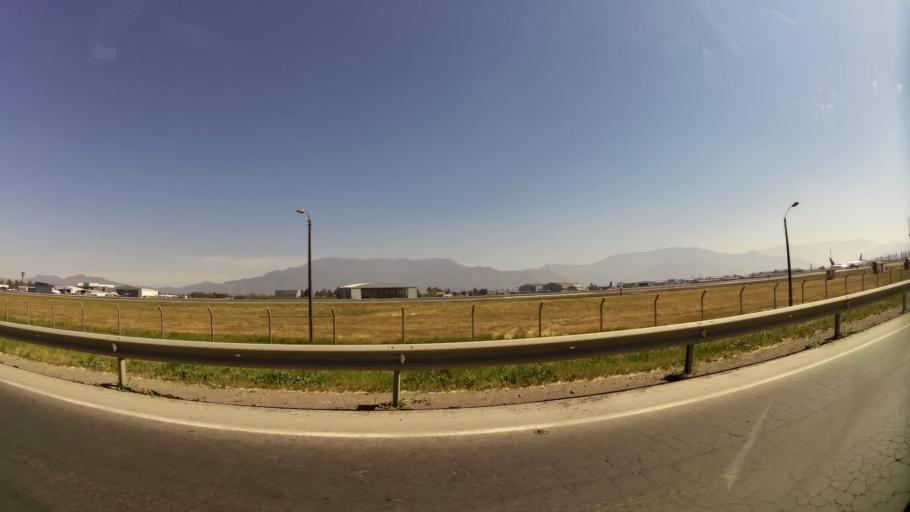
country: CL
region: Santiago Metropolitan
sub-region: Provincia de Santiago
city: Lo Prado
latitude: -33.3801
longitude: -70.7842
